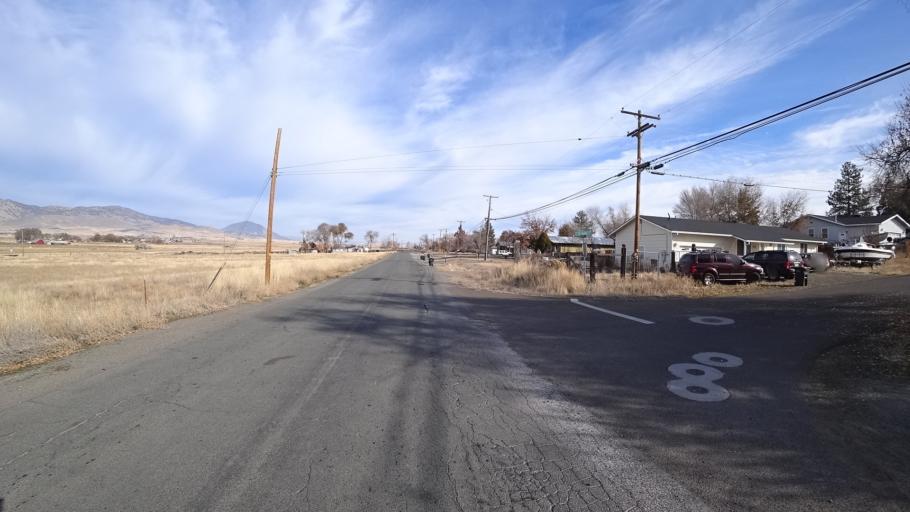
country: US
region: California
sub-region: Siskiyou County
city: Montague
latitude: 41.7328
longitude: -122.5206
